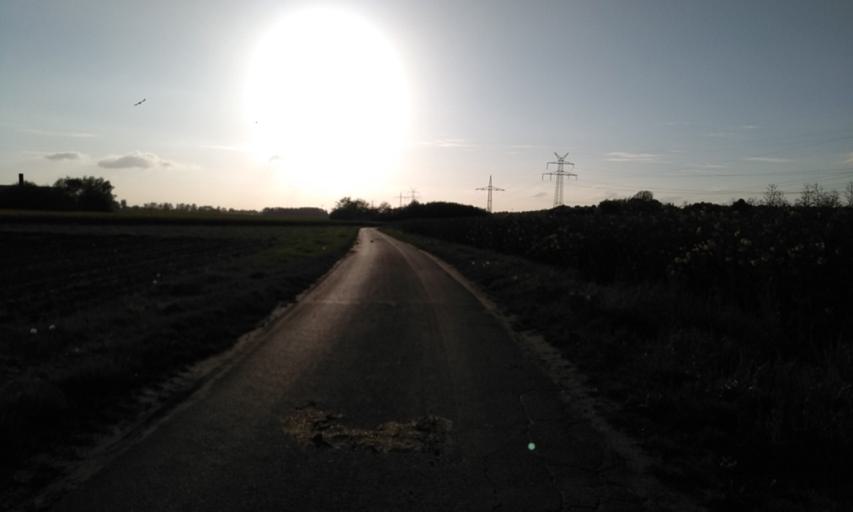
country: DE
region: Lower Saxony
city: Harsefeld
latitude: 53.4078
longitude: 9.5082
